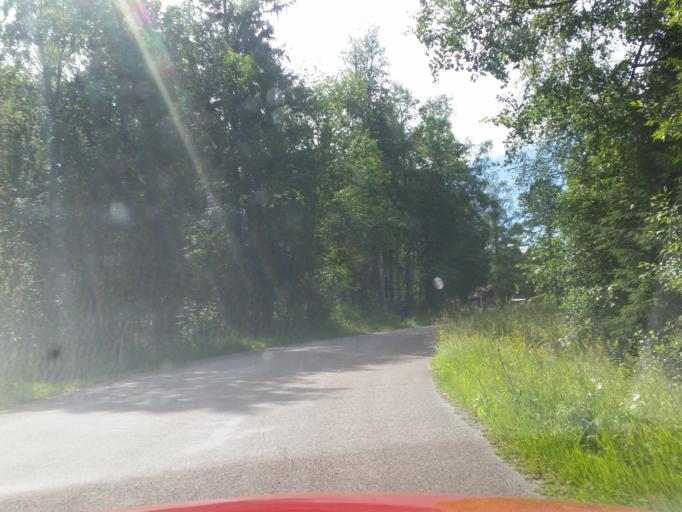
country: SE
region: Dalarna
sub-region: Gagnefs Kommun
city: Gagnef
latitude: 60.6610
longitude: 15.1216
